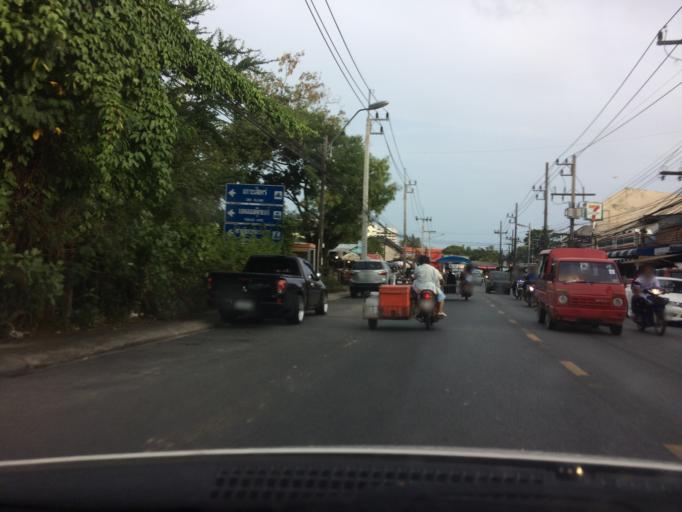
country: TH
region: Phuket
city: Ban Talat Yai
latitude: 7.8864
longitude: 98.4039
